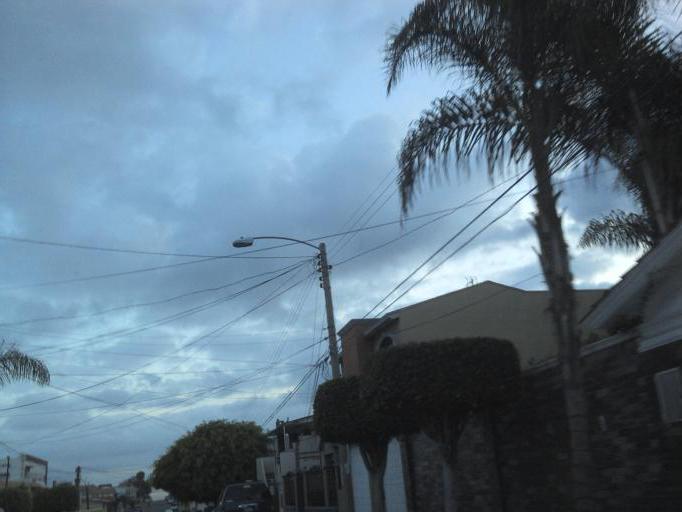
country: MX
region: Baja California
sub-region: Tijuana
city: La Esperanza [Granjas Familiares]
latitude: 32.5101
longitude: -117.1162
